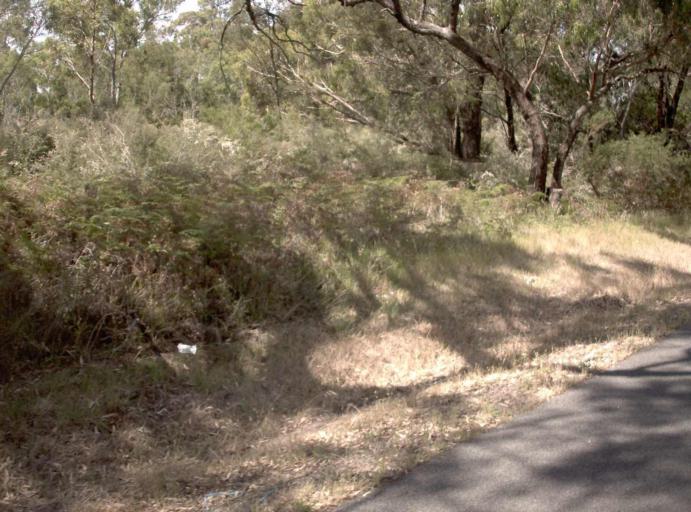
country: AU
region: Victoria
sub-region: Wellington
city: Sale
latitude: -37.9363
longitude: 147.1631
